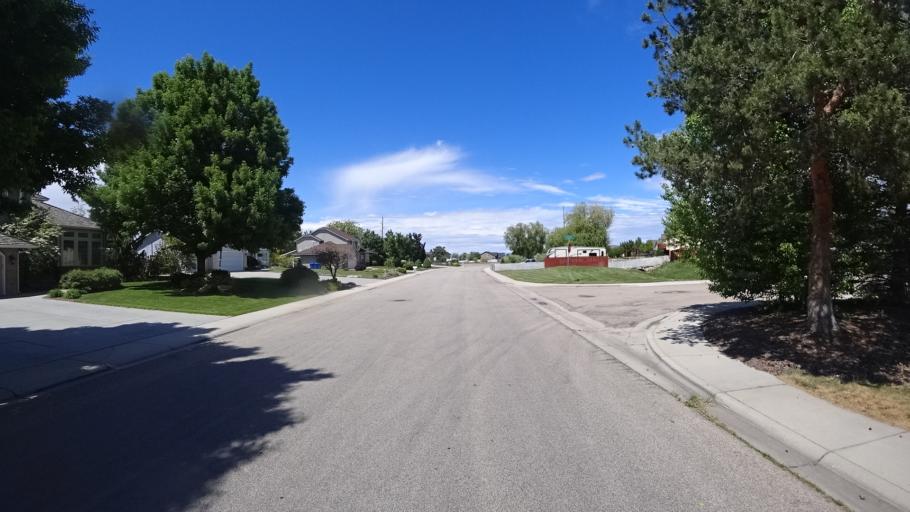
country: US
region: Idaho
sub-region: Ada County
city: Meridian
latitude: 43.5746
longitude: -116.3258
